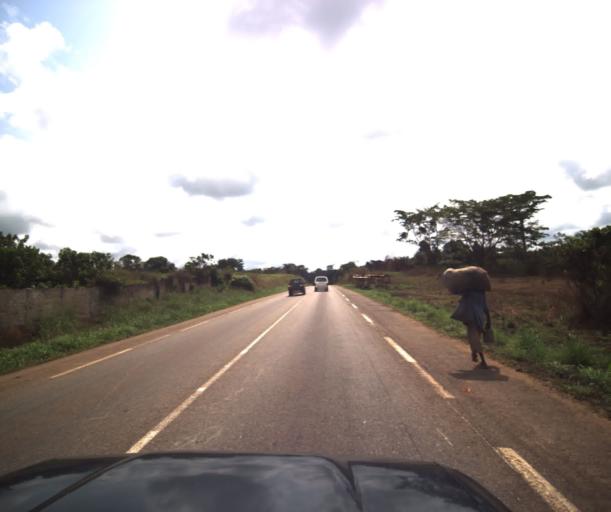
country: CM
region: Centre
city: Eseka
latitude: 3.8561
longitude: 10.5741
